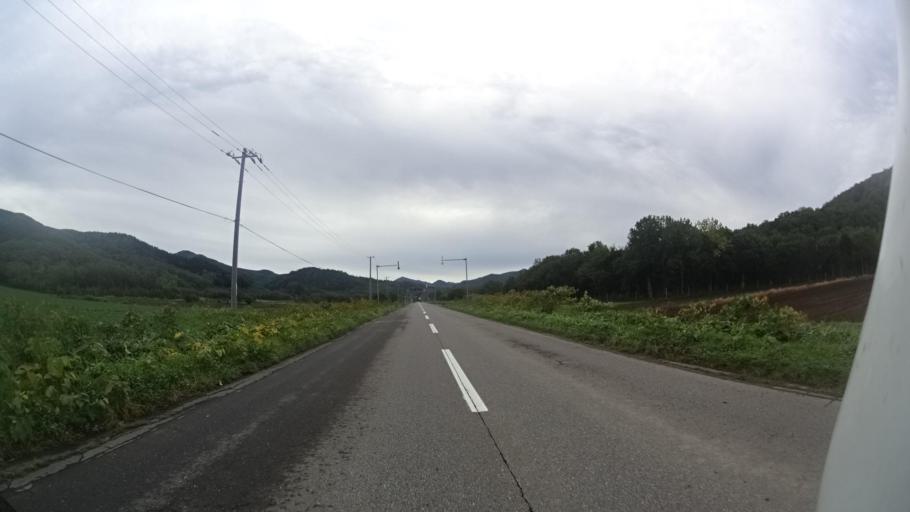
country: JP
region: Hokkaido
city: Shibetsu
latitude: 43.8461
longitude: 144.7793
